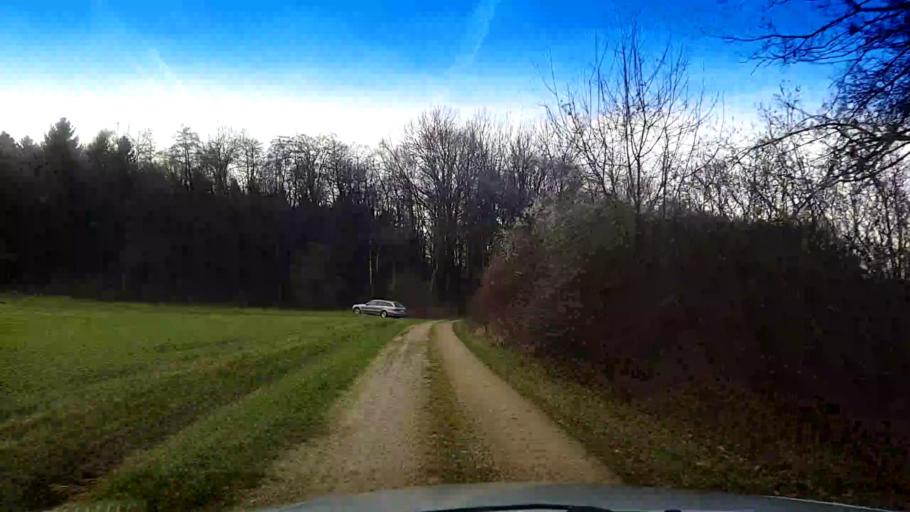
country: DE
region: Bavaria
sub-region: Upper Franconia
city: Schesslitz
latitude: 49.9922
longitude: 11.0318
